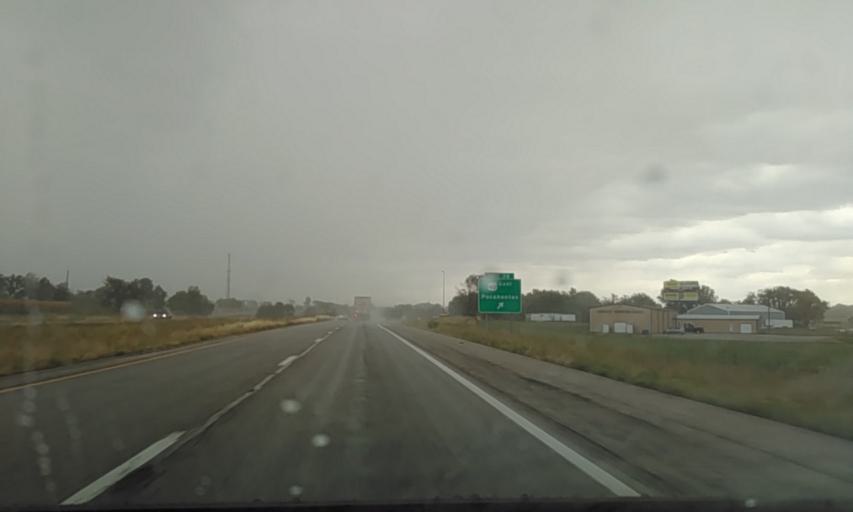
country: US
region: Illinois
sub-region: Madison County
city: Highland
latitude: 38.8281
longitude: -89.5510
